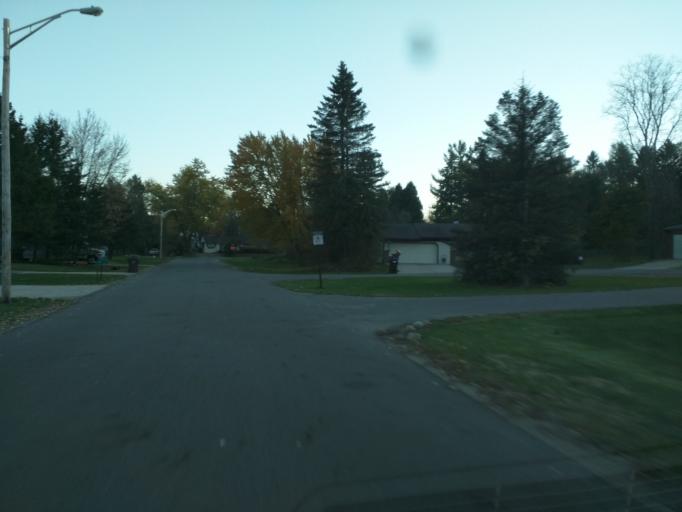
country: US
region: Michigan
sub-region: Eaton County
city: Waverly
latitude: 42.7399
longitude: -84.6070
